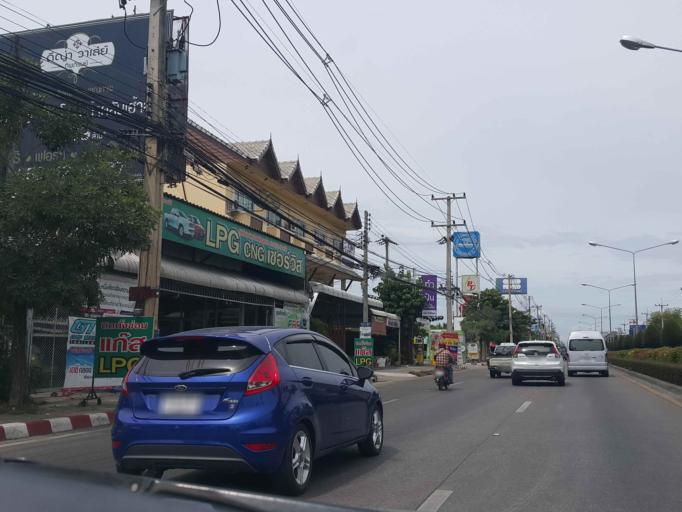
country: TH
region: Chiang Mai
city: Chiang Mai
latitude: 18.7408
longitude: 98.9578
